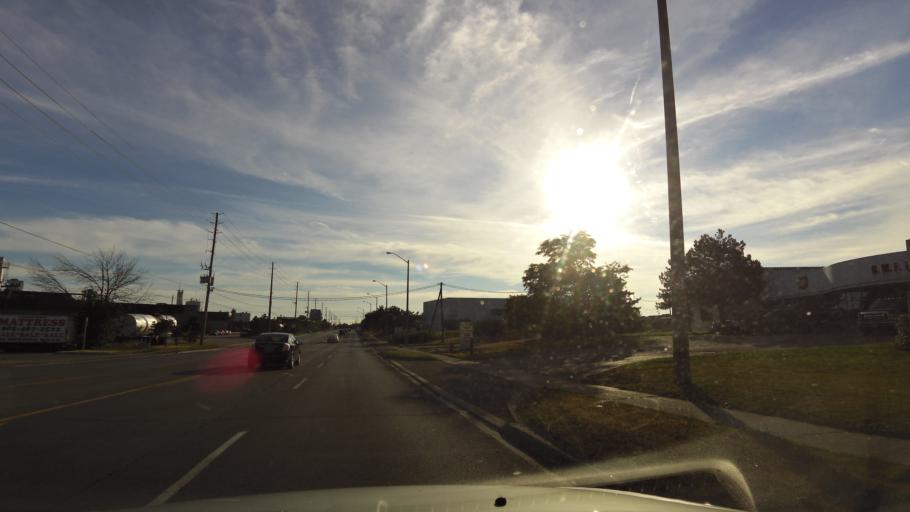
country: CA
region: Ontario
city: Brampton
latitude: 43.6947
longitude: -79.7353
